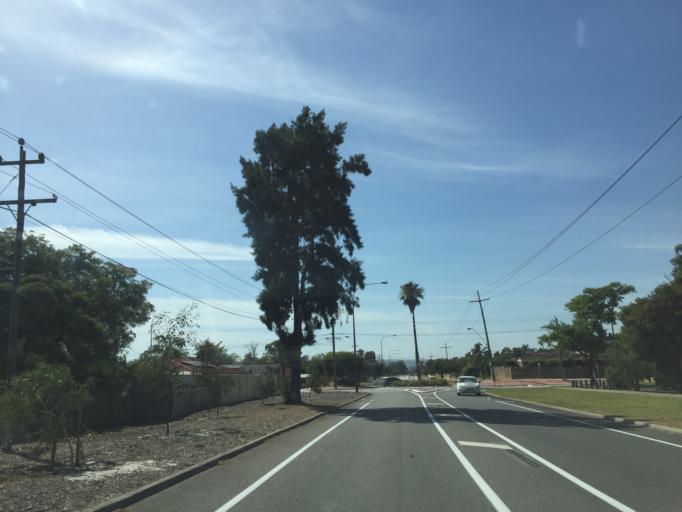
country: AU
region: Western Australia
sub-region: Gosnells
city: Thornlie
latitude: -32.0777
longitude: 115.9643
